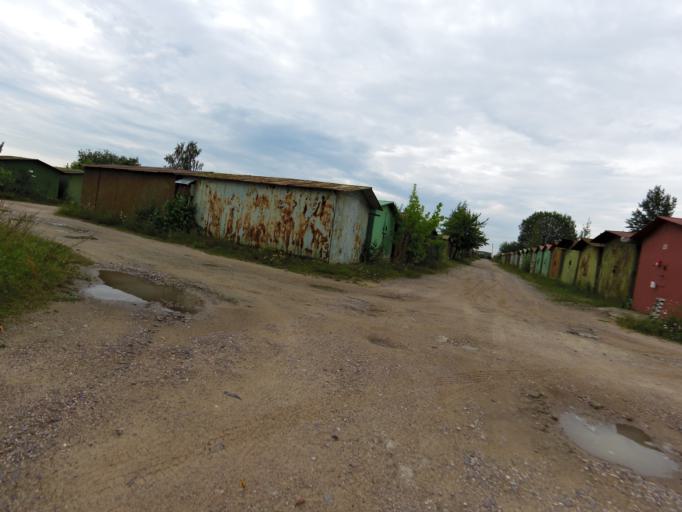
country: LT
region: Vilnius County
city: Pilaite
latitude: 54.7010
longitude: 25.2008
